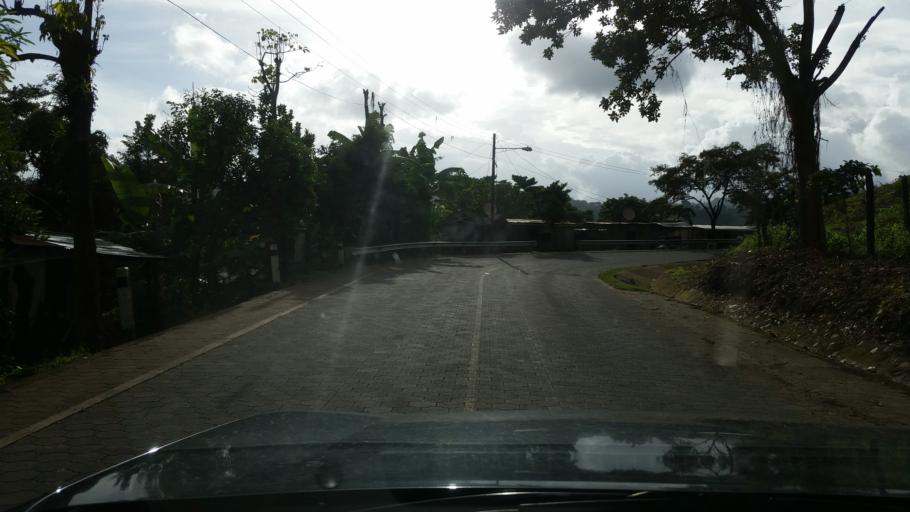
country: NI
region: Matagalpa
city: San Ramon
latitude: 13.1467
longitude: -85.7359
